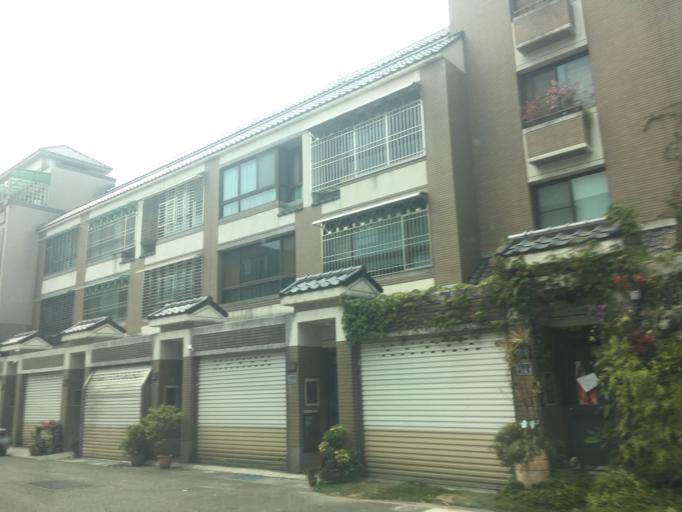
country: TW
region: Taiwan
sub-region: Taichung City
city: Taichung
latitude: 24.1849
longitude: 120.6830
